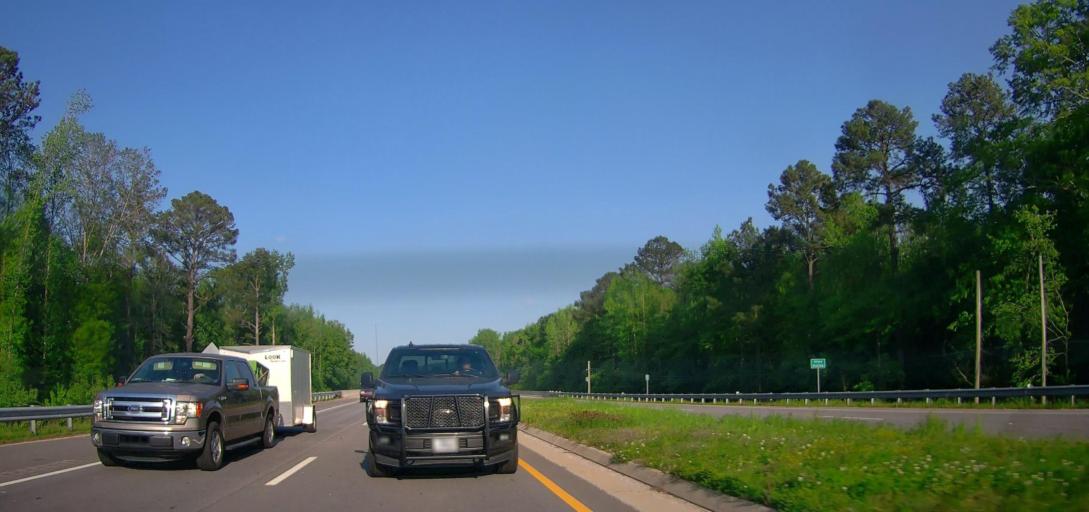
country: US
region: Georgia
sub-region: Newton County
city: Covington
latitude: 33.5934
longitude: -83.8129
